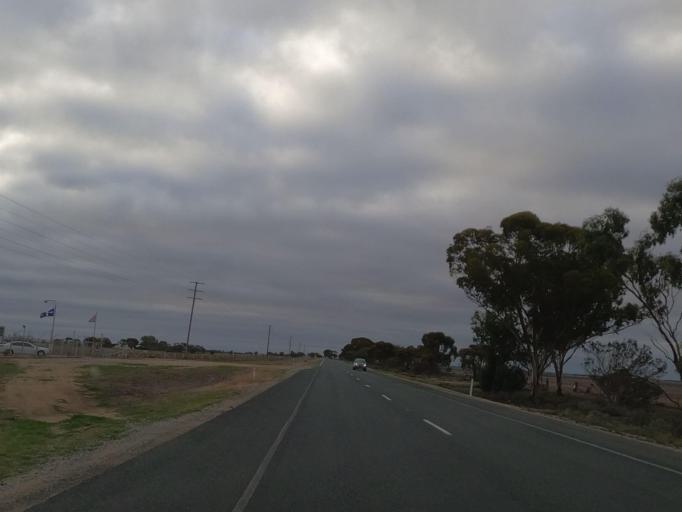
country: AU
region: Victoria
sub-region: Swan Hill
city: Swan Hill
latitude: -35.5819
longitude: 143.7896
